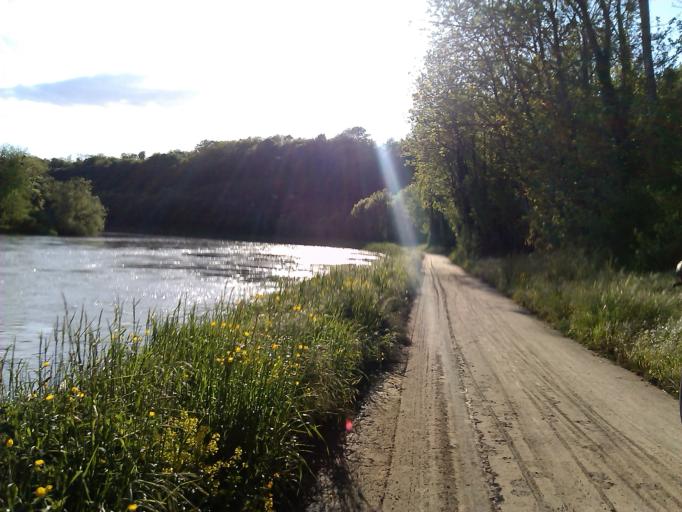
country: FR
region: Franche-Comte
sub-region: Departement du Doubs
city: Clerval
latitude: 47.4165
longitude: 6.5196
